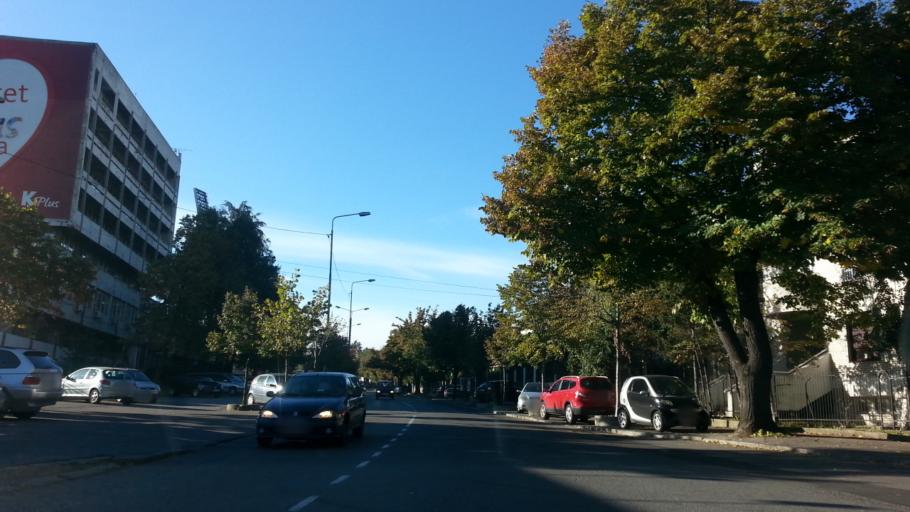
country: RS
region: Central Serbia
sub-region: Belgrade
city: Savski Venac
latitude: 44.7858
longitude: 20.4630
